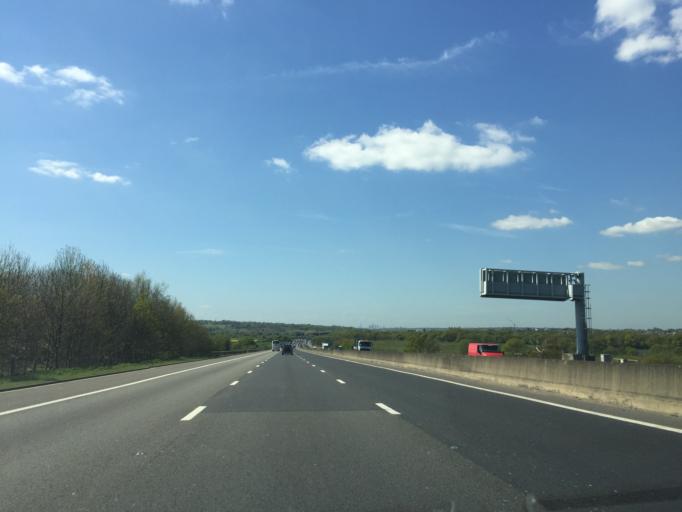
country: GB
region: England
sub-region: Essex
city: Theydon Bois
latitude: 51.6618
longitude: 0.1111
